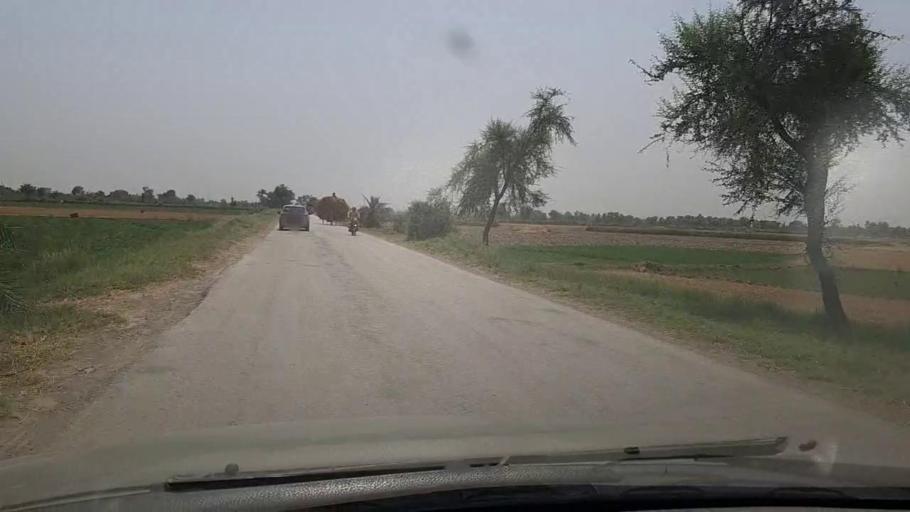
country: PK
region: Sindh
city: Kambar
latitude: 27.6192
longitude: 68.0210
